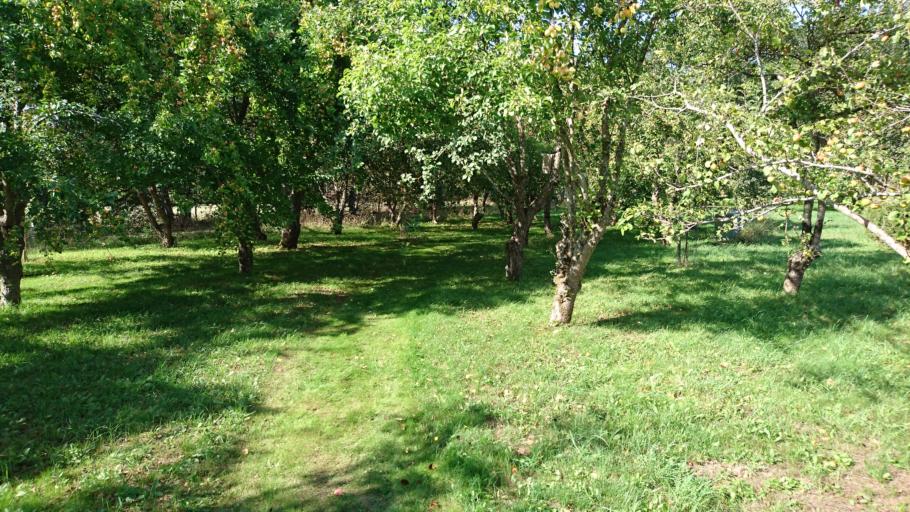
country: DK
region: North Denmark
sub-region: Frederikshavn Kommune
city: Saeby
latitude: 57.3444
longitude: 10.5046
